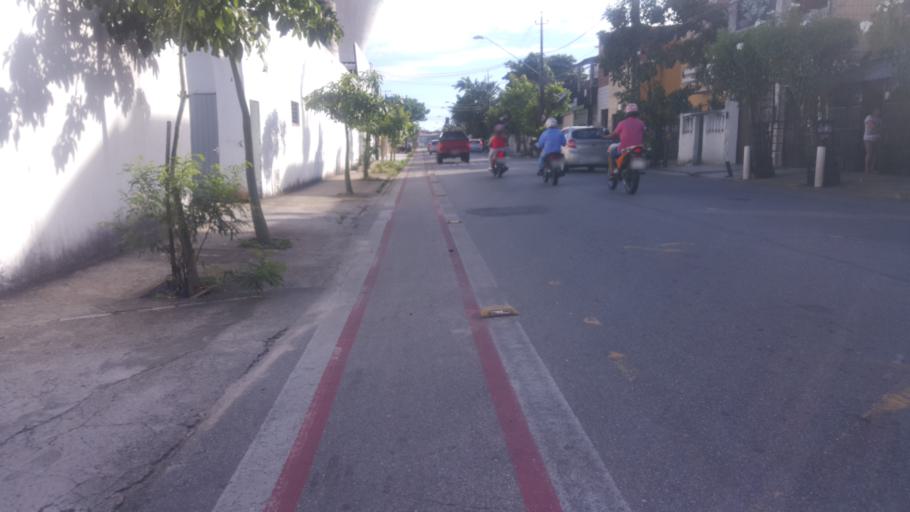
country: BR
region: Ceara
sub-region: Fortaleza
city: Fortaleza
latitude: -3.7540
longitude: -38.5399
